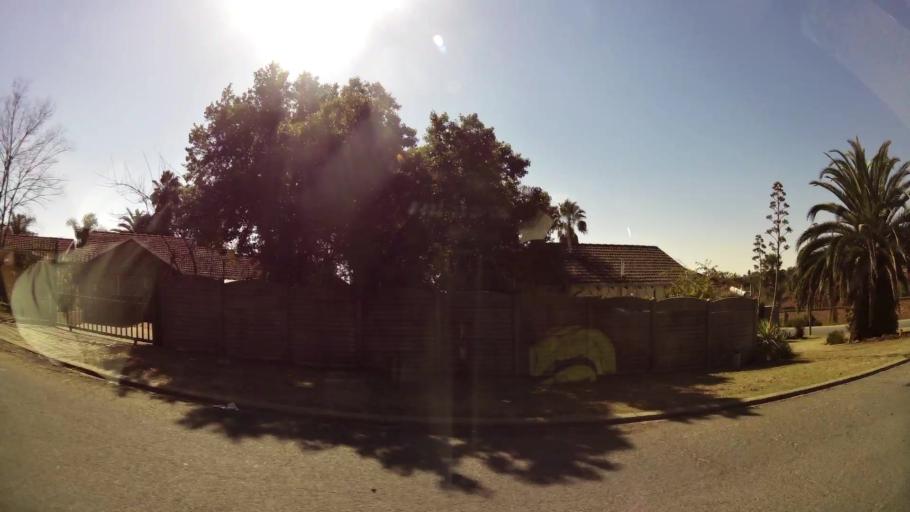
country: ZA
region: Gauteng
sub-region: Ekurhuleni Metropolitan Municipality
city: Tembisa
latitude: -26.0520
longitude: 28.2206
